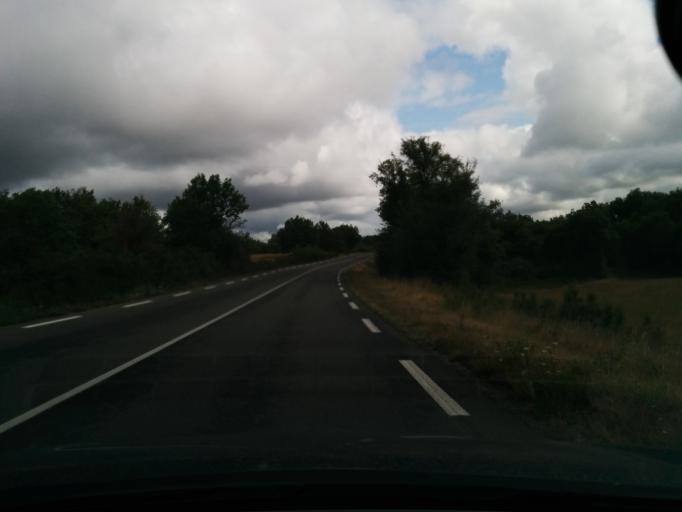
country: FR
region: Midi-Pyrenees
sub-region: Departement du Lot
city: Souillac
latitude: 44.9659
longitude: 1.5027
